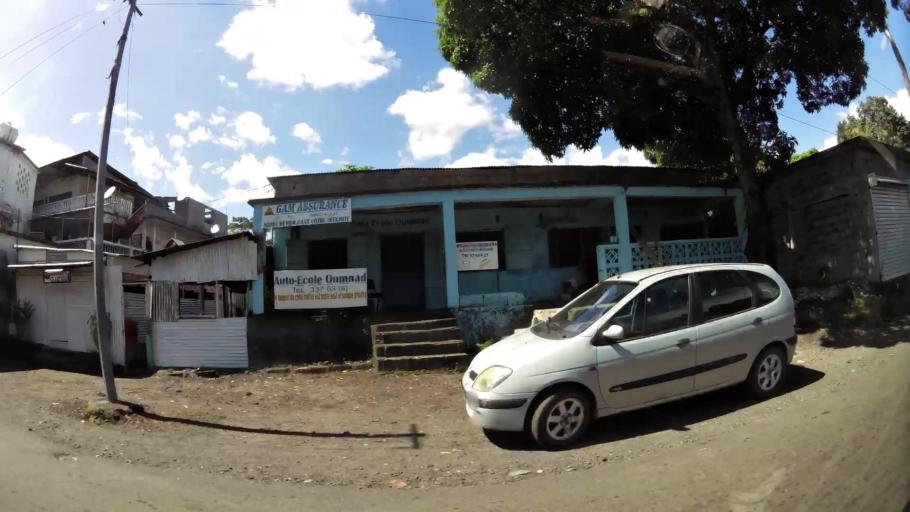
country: KM
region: Grande Comore
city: Mavingouni
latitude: -11.7186
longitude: 43.2508
